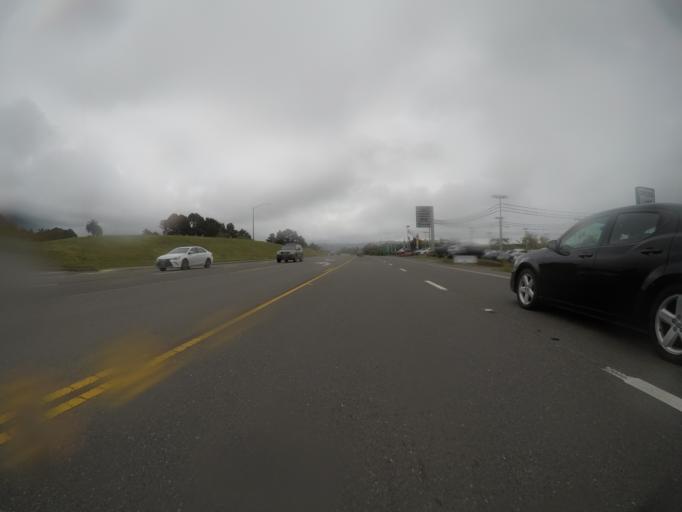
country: US
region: California
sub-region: Humboldt County
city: Bayview
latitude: 40.7671
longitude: -124.1917
